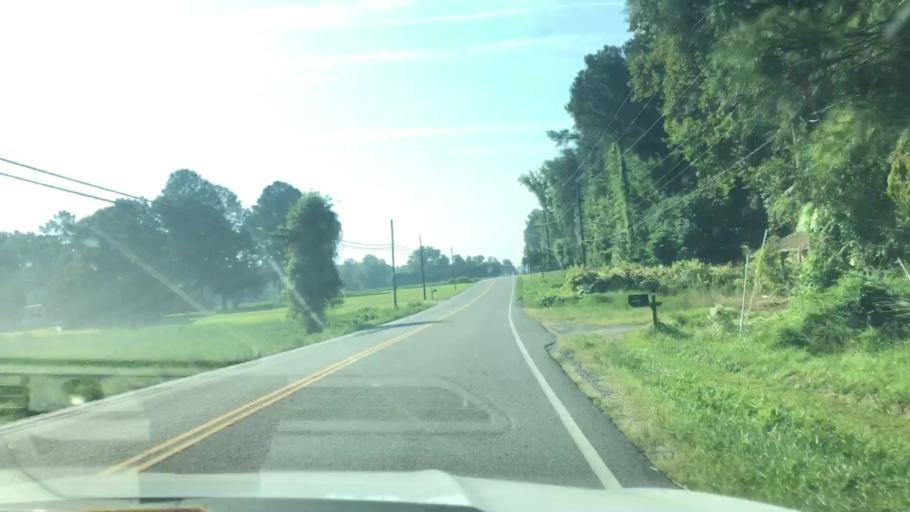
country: US
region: Virginia
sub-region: Richmond County
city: Warsaw
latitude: 37.8967
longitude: -76.6765
